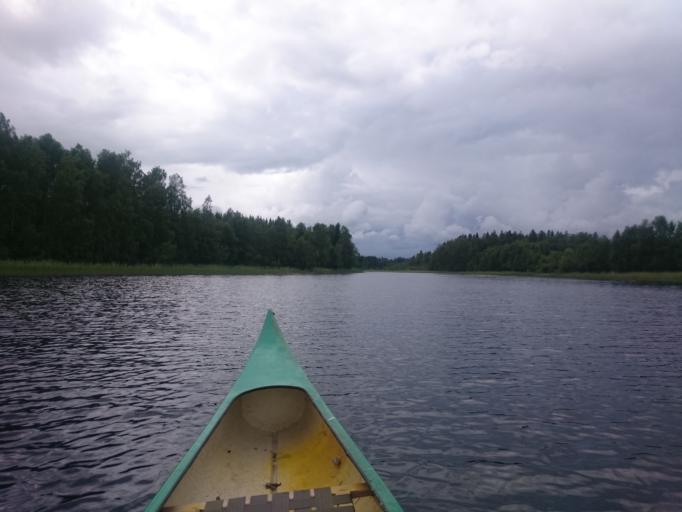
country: SE
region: Vaesternorrland
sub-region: OErnskoeldsviks Kommun
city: Ornskoldsvik
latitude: 63.6485
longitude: 18.6155
